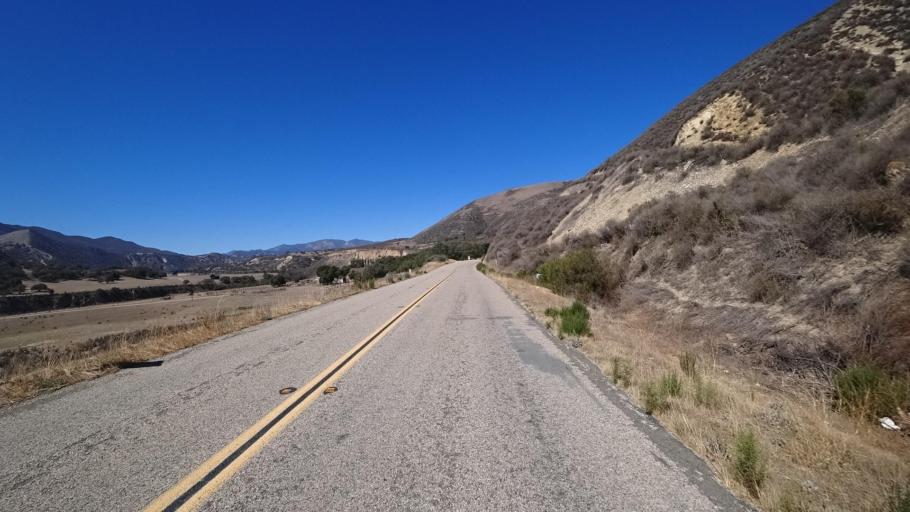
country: US
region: California
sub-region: Monterey County
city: Greenfield
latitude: 36.2700
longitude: -121.3378
